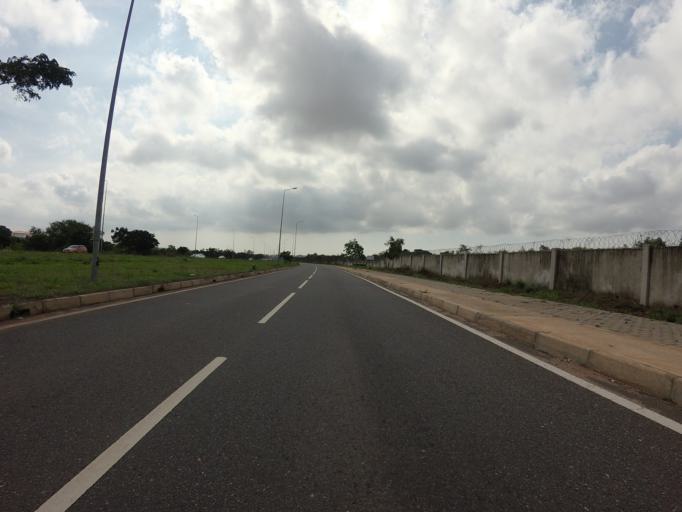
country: GH
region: Greater Accra
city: Teshi Old Town
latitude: 5.6125
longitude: -0.1511
